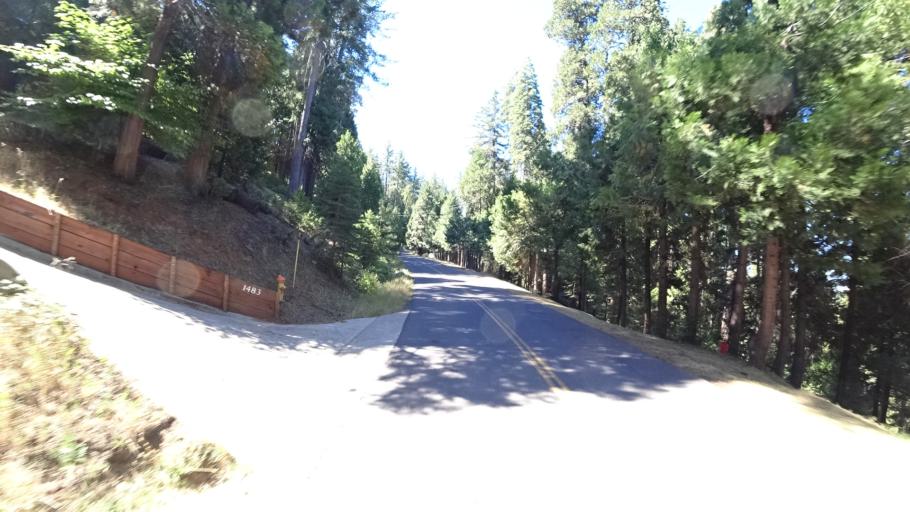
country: US
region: California
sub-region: Calaveras County
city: Arnold
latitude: 38.2487
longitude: -120.3279
